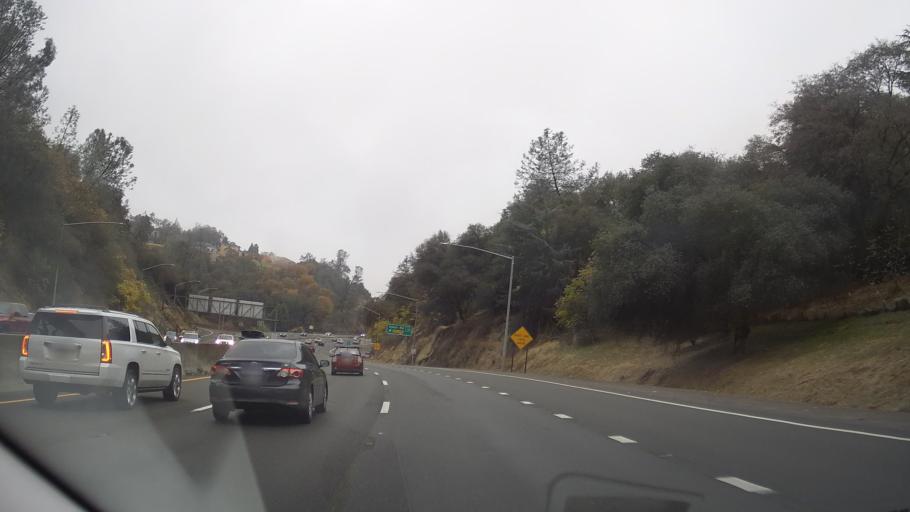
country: US
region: California
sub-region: Placer County
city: Auburn
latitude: 38.8956
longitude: -121.0821
